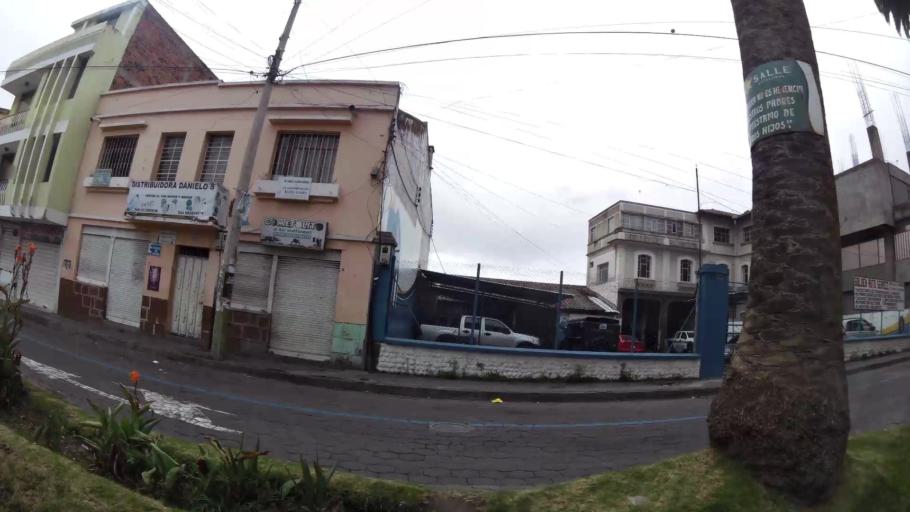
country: EC
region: Cotopaxi
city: Latacunga
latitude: -0.9358
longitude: -78.6172
